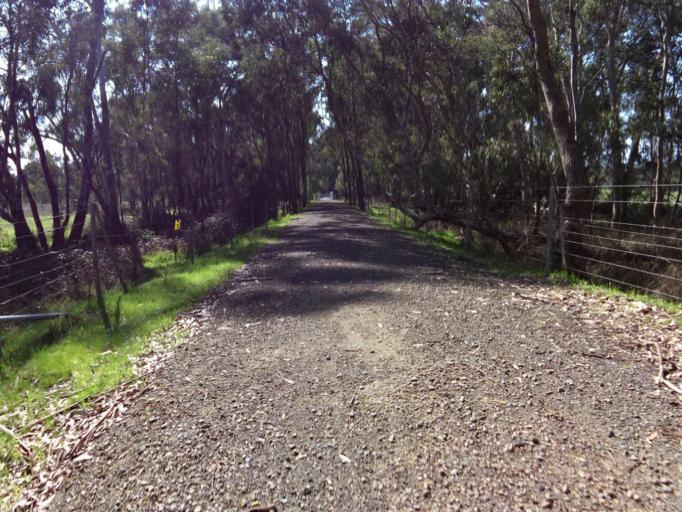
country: AU
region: Victoria
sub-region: Murrindindi
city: Alexandra
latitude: -37.1578
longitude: 145.5699
